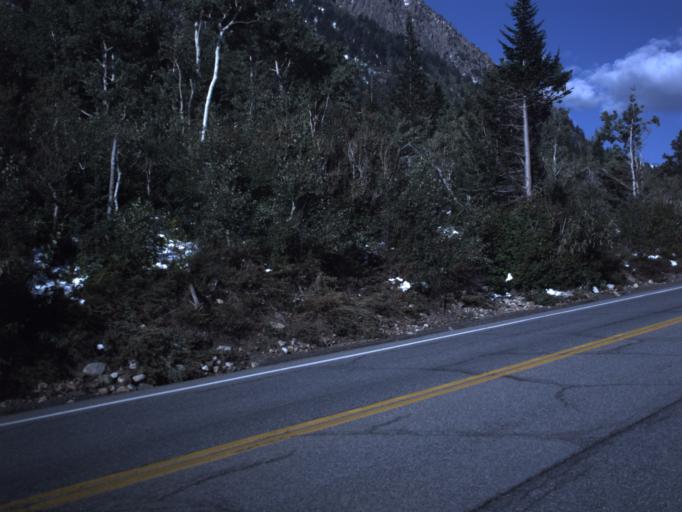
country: US
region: Utah
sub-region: Salt Lake County
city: Granite
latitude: 40.5761
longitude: -111.6793
